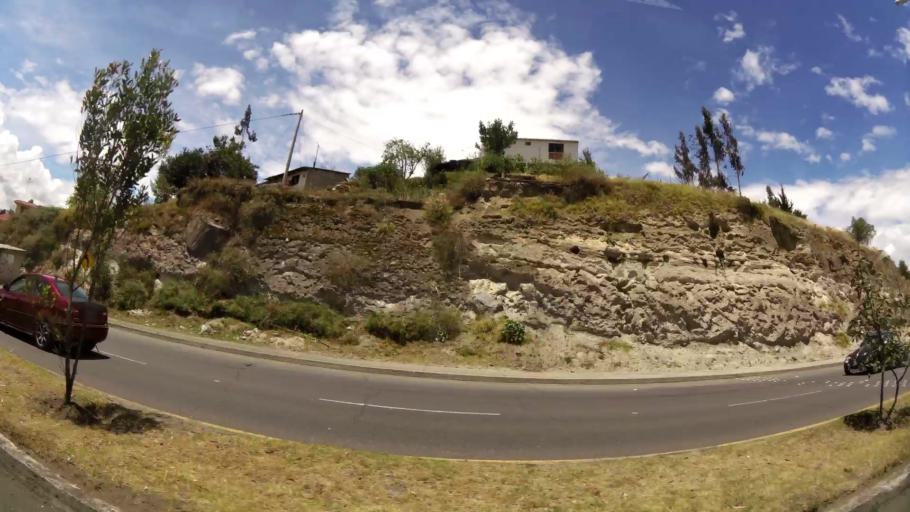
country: EC
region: Tungurahua
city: Pelileo
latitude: -1.3130
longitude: -78.5980
